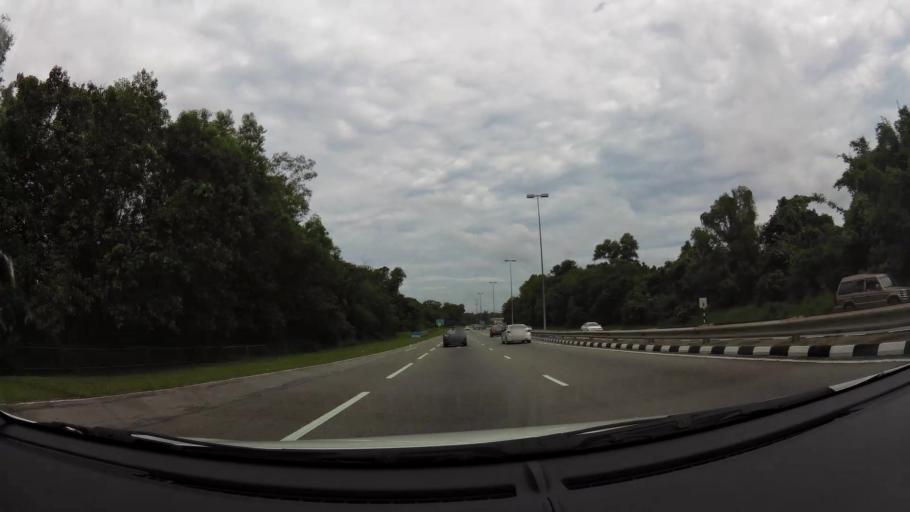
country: BN
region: Brunei and Muara
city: Bandar Seri Begawan
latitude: 4.9123
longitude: 114.9065
